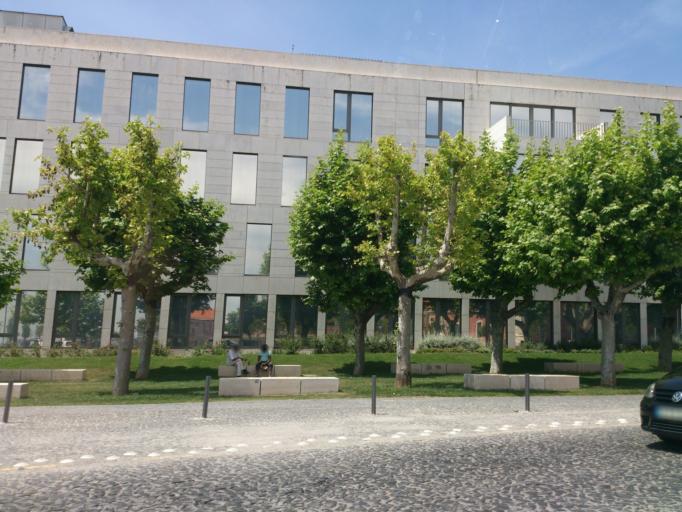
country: PT
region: Lisbon
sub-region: Lisbon
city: Lisbon
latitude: 38.7060
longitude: -9.1413
